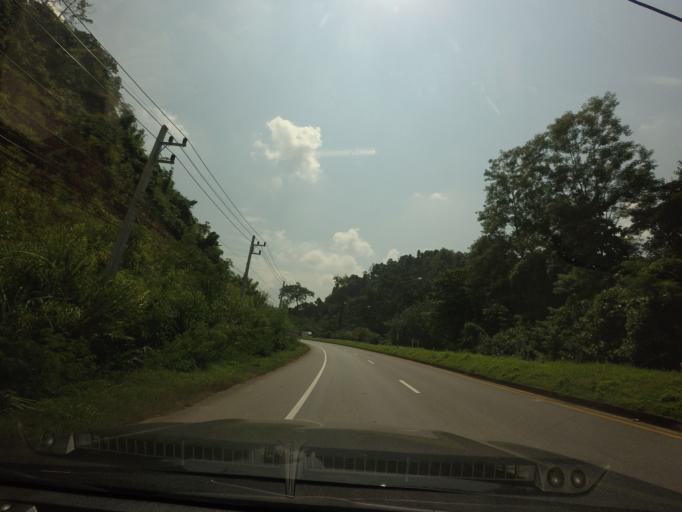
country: TH
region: Uttaradit
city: Lap Lae
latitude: 17.8063
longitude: 100.1091
